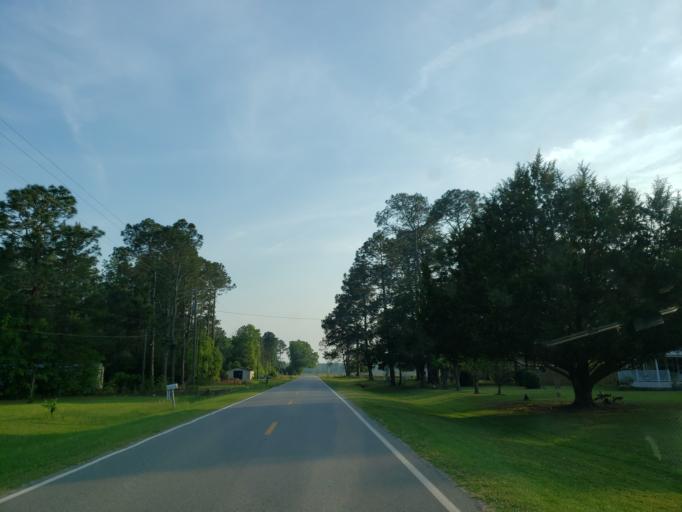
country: US
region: Georgia
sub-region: Cook County
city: Sparks
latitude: 31.2009
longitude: -83.4238
